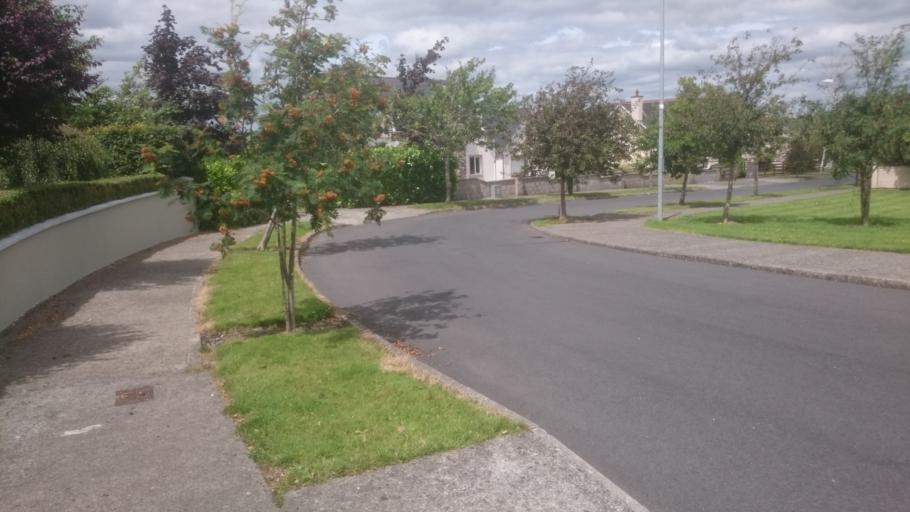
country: IE
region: Leinster
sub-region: Kilkenny
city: Callan
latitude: 52.5369
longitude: -7.2734
